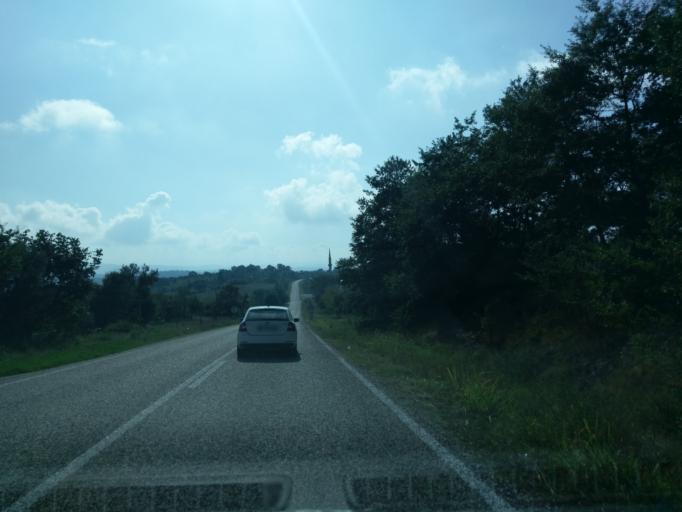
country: TR
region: Sinop
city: Erfelek
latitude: 41.9681
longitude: 34.8605
